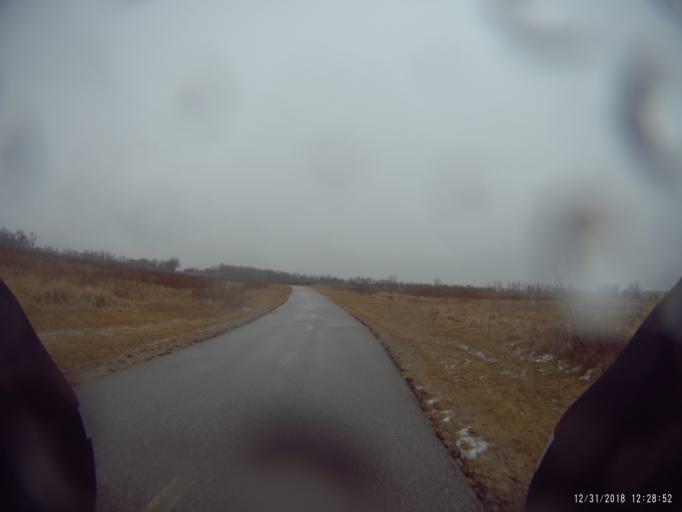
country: US
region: Wisconsin
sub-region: Dane County
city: Verona
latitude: 42.9983
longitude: -89.5170
